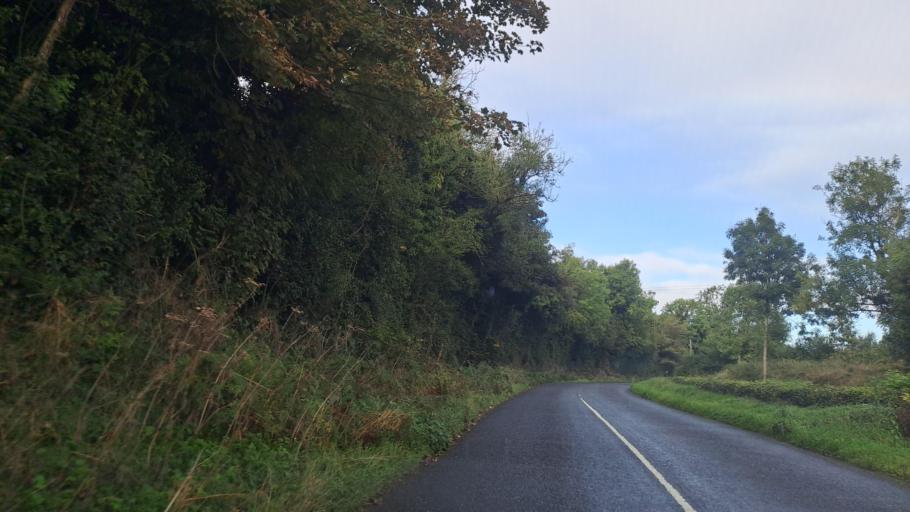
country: IE
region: Ulster
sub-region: County Monaghan
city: Carrickmacross
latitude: 53.9627
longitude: -6.6904
